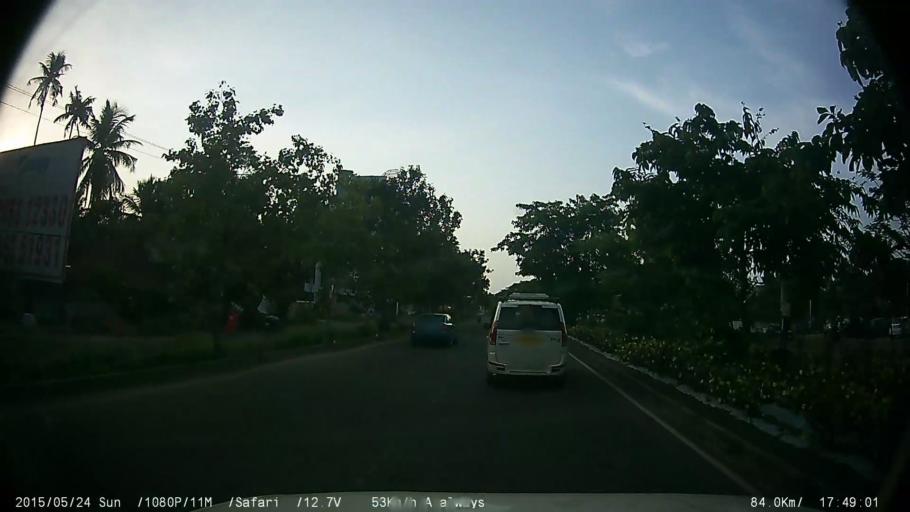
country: IN
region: Kerala
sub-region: Ernakulam
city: Cochin
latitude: 9.9873
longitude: 76.3159
